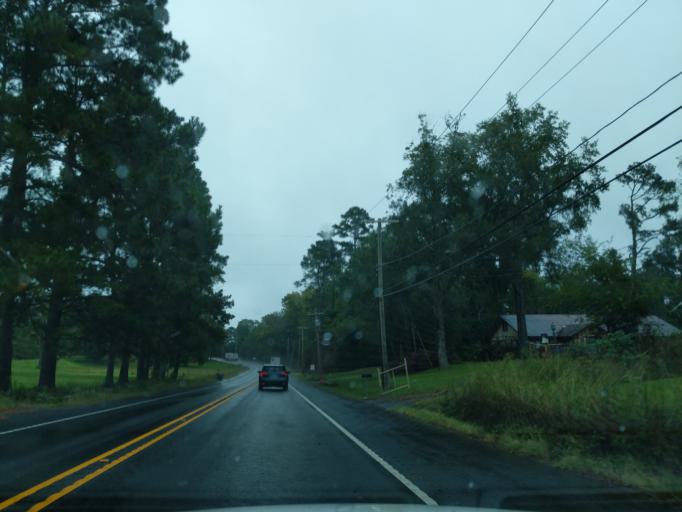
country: US
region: Louisiana
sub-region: Caddo Parish
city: Greenwood
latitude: 32.3736
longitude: -94.0382
